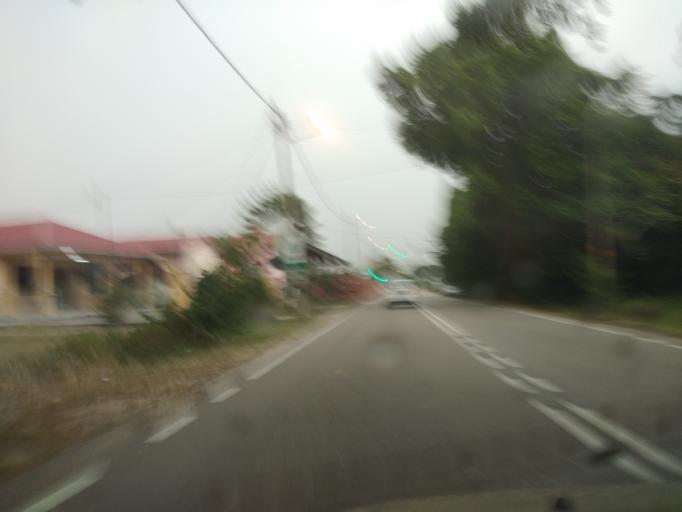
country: MY
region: Penang
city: Permatang Kuching
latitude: 5.4790
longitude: 100.4014
